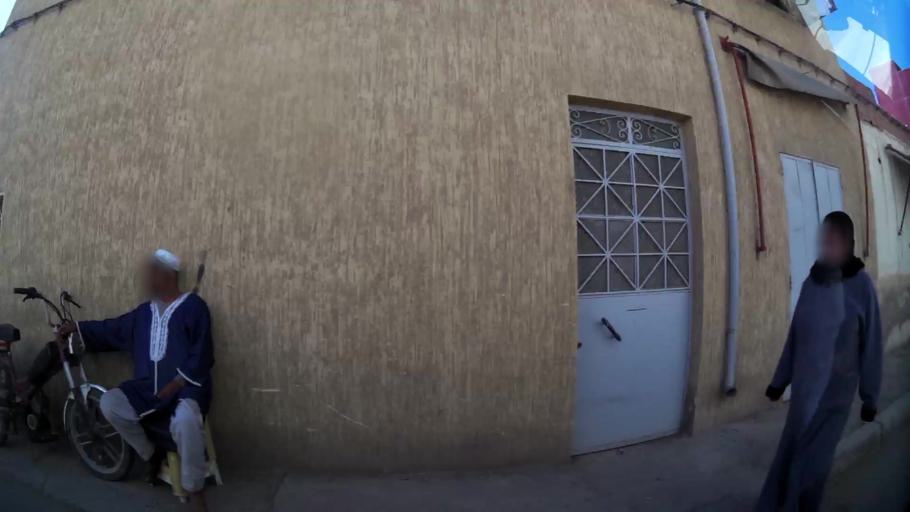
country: MA
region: Oriental
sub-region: Oujda-Angad
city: Oujda
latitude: 34.6817
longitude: -1.9351
